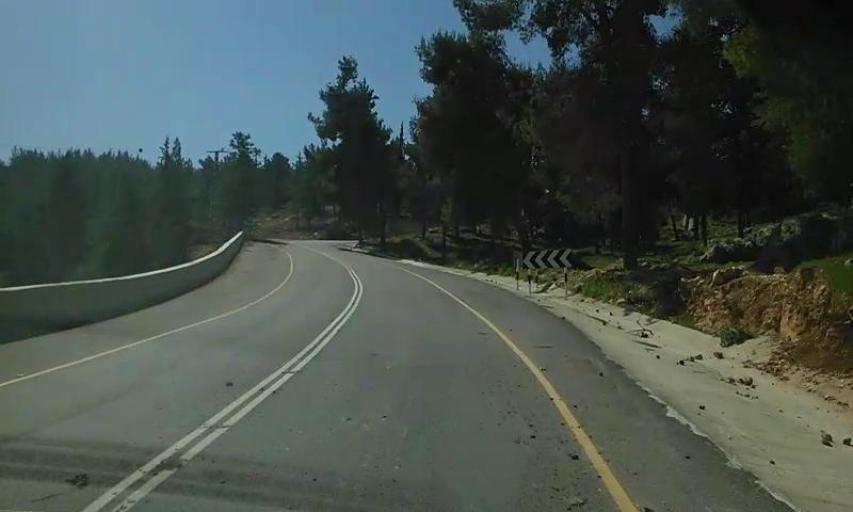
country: PS
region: West Bank
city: Nahhalin
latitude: 31.6763
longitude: 35.1082
